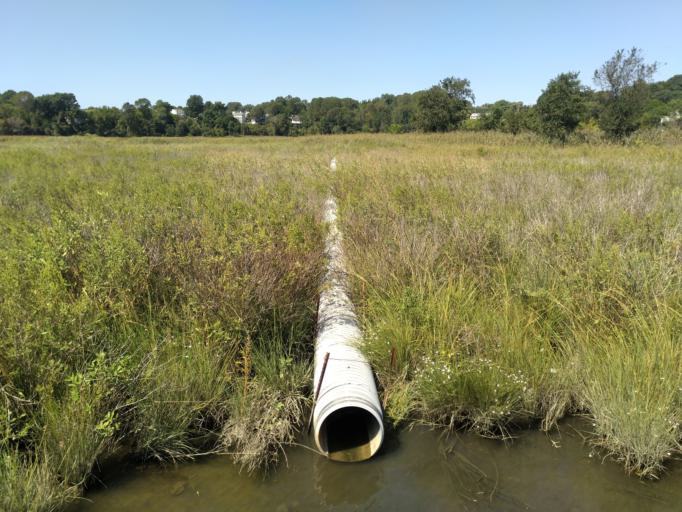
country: US
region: Maryland
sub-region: Calvert County
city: Chesapeake Beach
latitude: 38.6903
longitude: -76.5385
